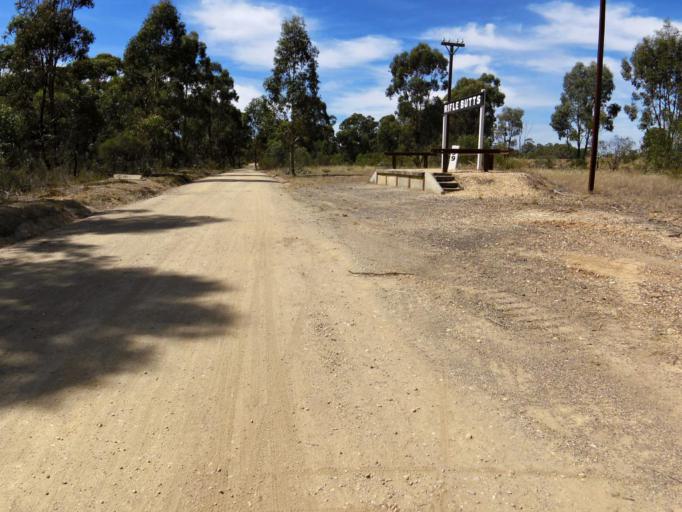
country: AU
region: Victoria
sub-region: Greater Bendigo
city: White Hills
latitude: -36.7547
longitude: 144.3263
